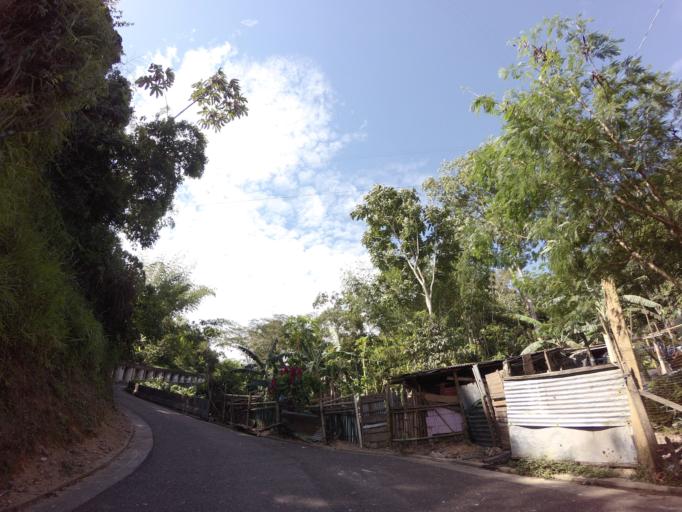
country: CO
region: Caldas
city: Norcasia
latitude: 5.5737
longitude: -74.8983
